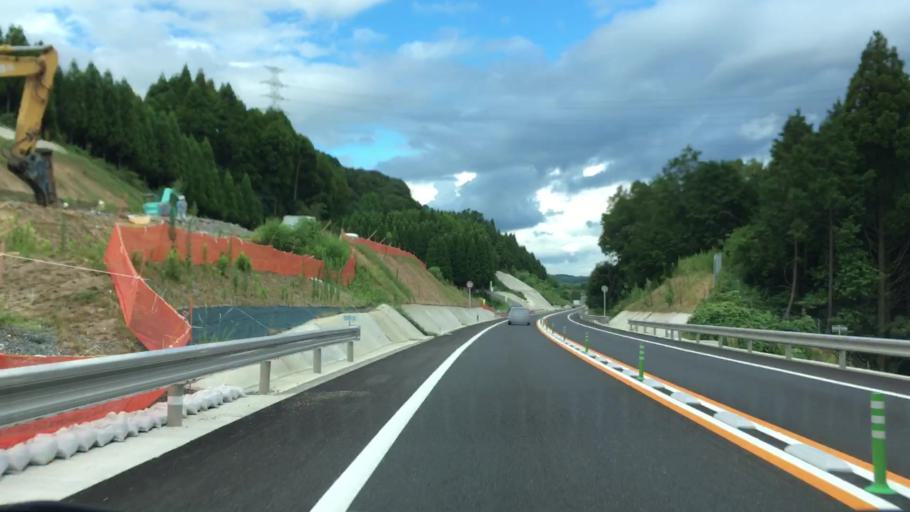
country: JP
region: Saga Prefecture
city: Imaricho-ko
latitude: 33.3141
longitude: 129.9188
